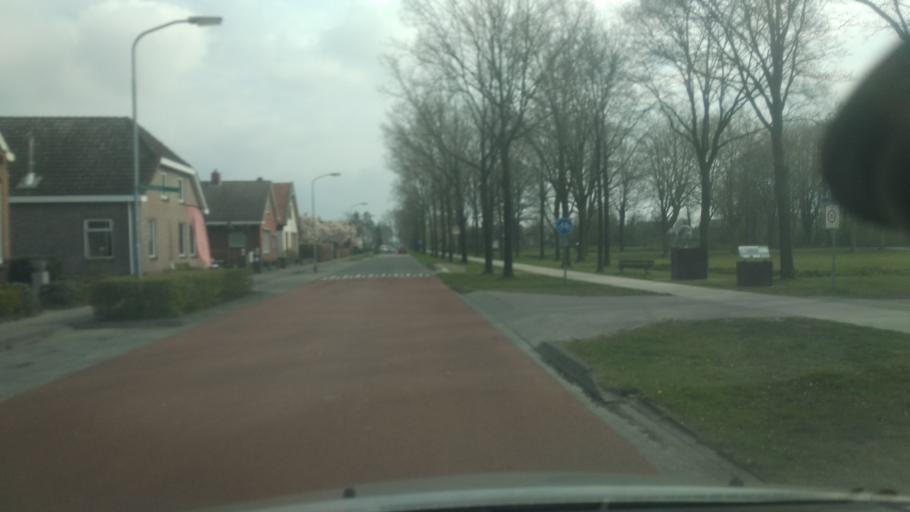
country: NL
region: Groningen
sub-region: Gemeente Stadskanaal
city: Stadskanaal
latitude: 52.9021
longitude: 6.9187
